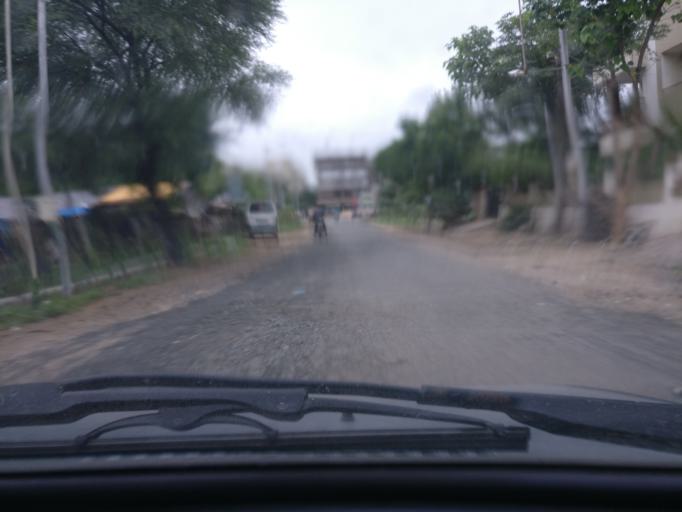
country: IN
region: Gujarat
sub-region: Ahmadabad
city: Naroda
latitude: 23.0553
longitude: 72.6638
